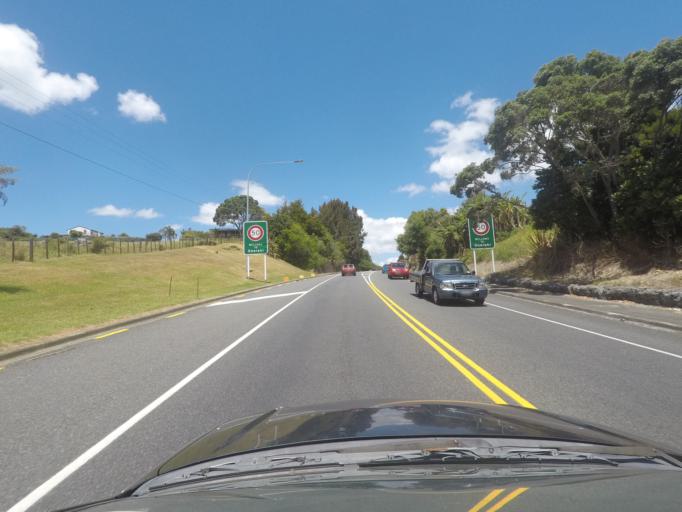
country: NZ
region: Northland
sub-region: Whangarei
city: Whangarei
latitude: -35.7431
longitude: 174.3658
